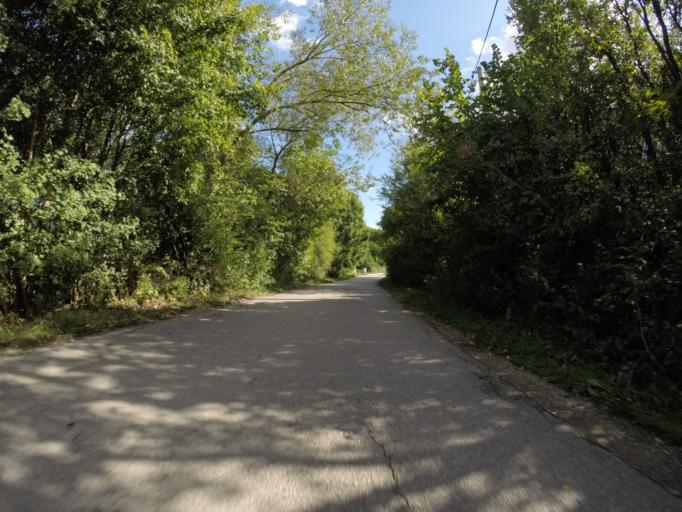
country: CZ
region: Zlin
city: Strani
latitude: 48.8375
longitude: 17.7603
